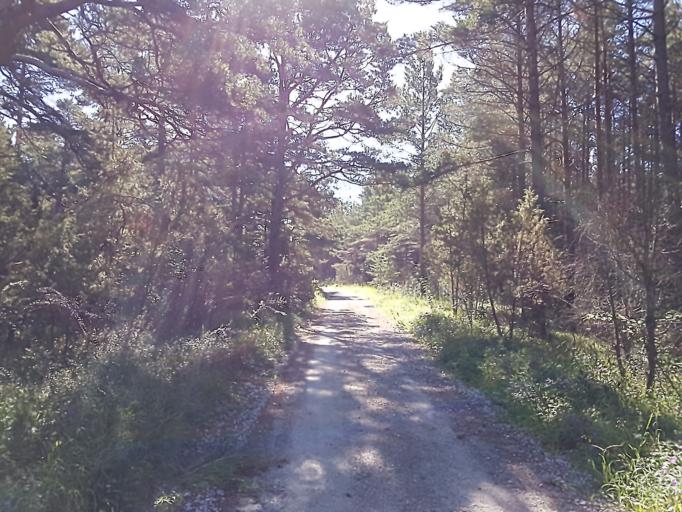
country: SE
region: Gotland
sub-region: Gotland
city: Visby
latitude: 57.6134
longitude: 18.3561
